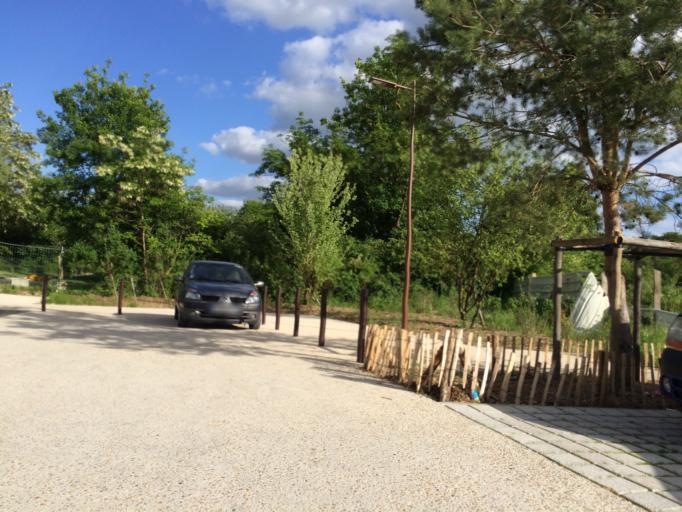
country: FR
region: Ile-de-France
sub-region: Departement de l'Essonne
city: Ris-Orangis
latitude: 48.6574
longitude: 2.4184
